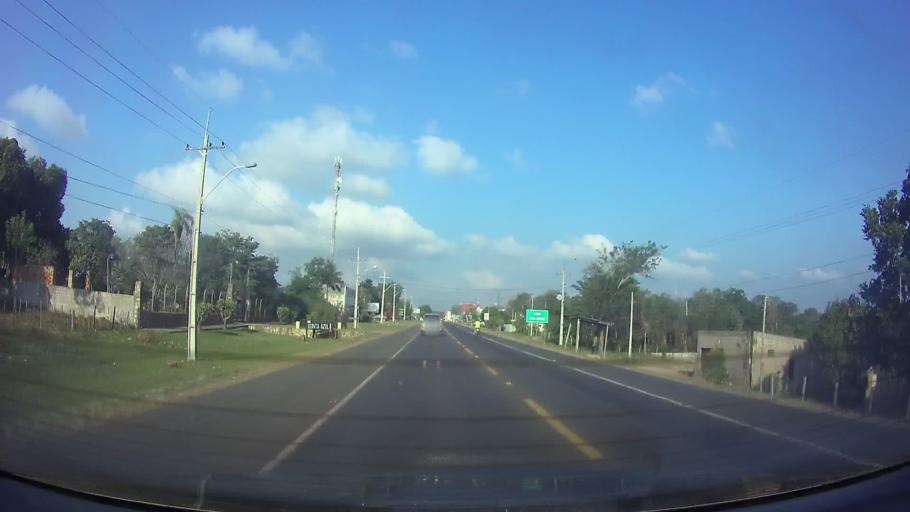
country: PY
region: Cordillera
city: Emboscada
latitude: -25.1217
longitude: -57.3622
